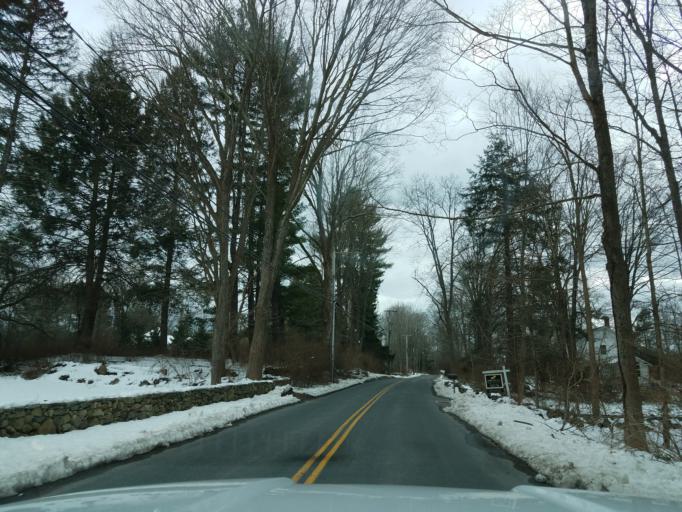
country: US
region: Connecticut
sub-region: Litchfield County
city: New Milford
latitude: 41.6168
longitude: -73.4300
